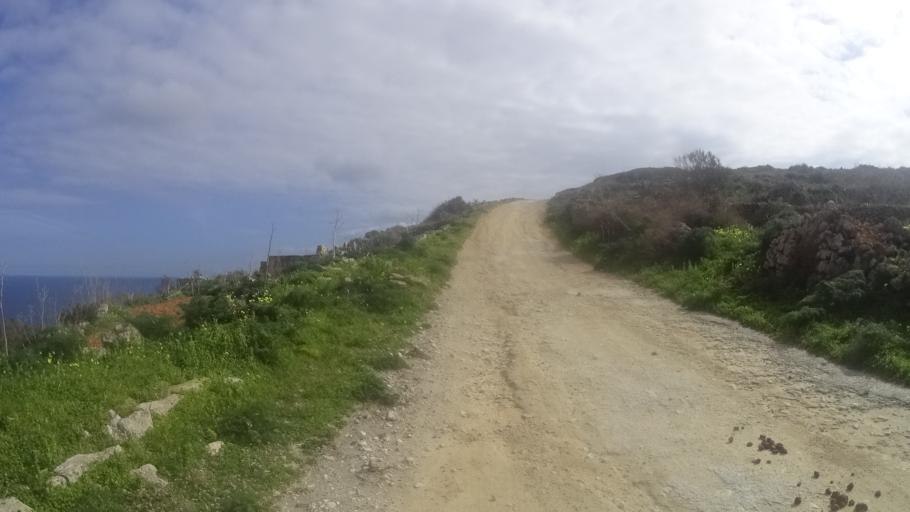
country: MT
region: Il-Qala
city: Qala
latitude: 36.0430
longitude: 14.3170
